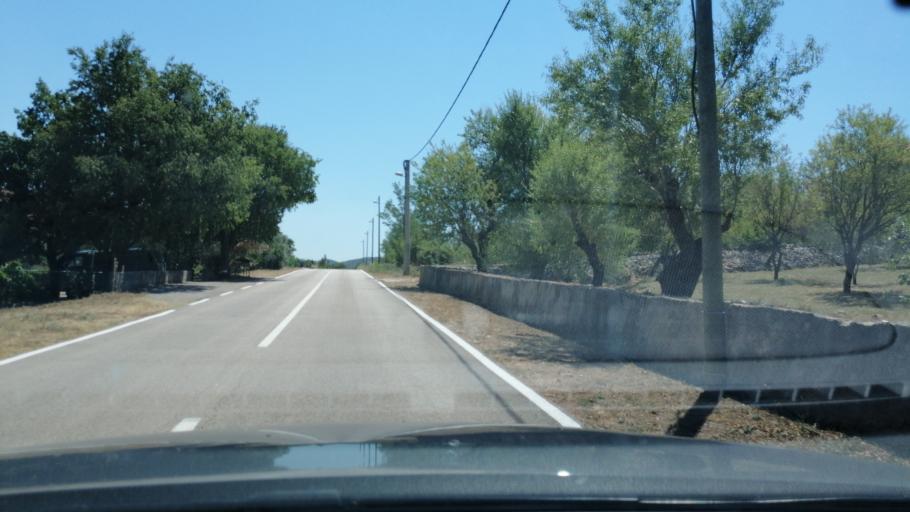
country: HR
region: Sibensko-Kniniska
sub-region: Grad Sibenik
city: Pirovac
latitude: 43.8694
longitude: 15.6814
